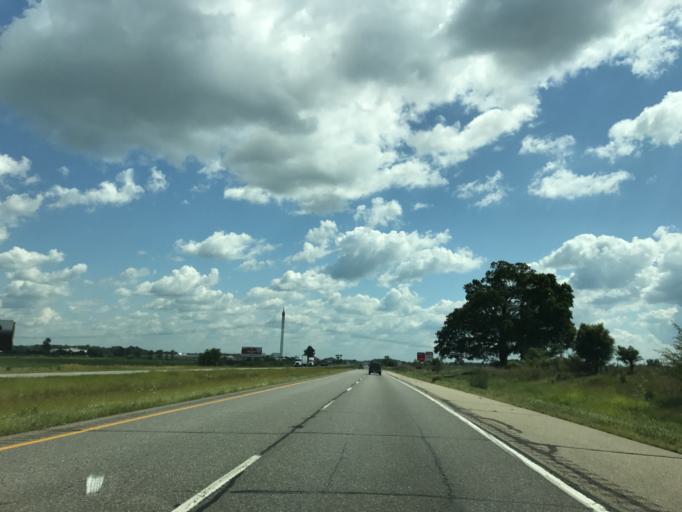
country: US
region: Indiana
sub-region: Marshall County
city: Plymouth
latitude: 41.3612
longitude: -86.3652
